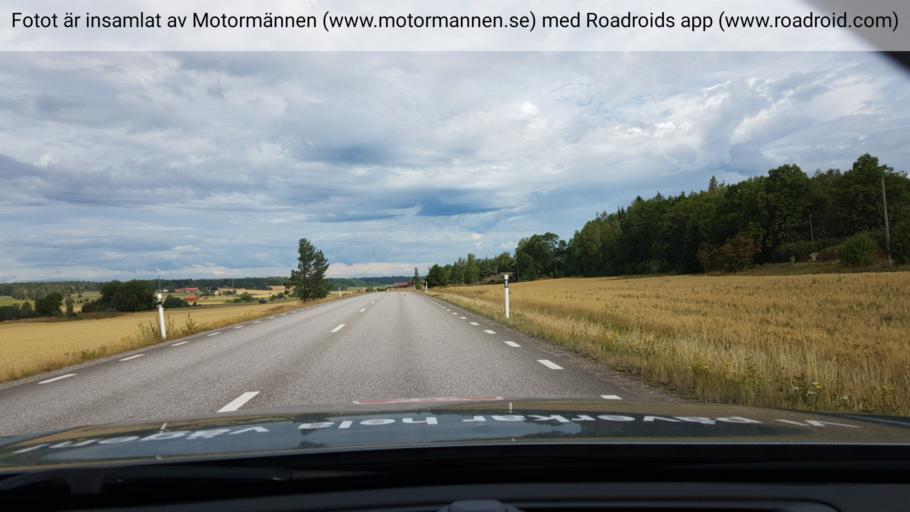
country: SE
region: Uppsala
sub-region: Heby Kommun
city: Morgongava
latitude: 59.8872
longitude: 16.9110
